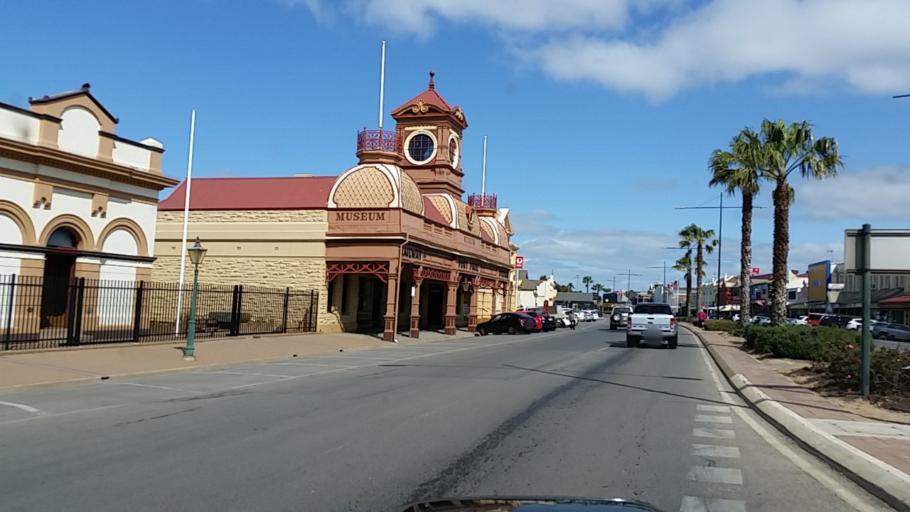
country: AU
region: South Australia
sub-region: Port Pirie City and Dists
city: Port Pirie
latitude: -33.1754
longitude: 138.0101
